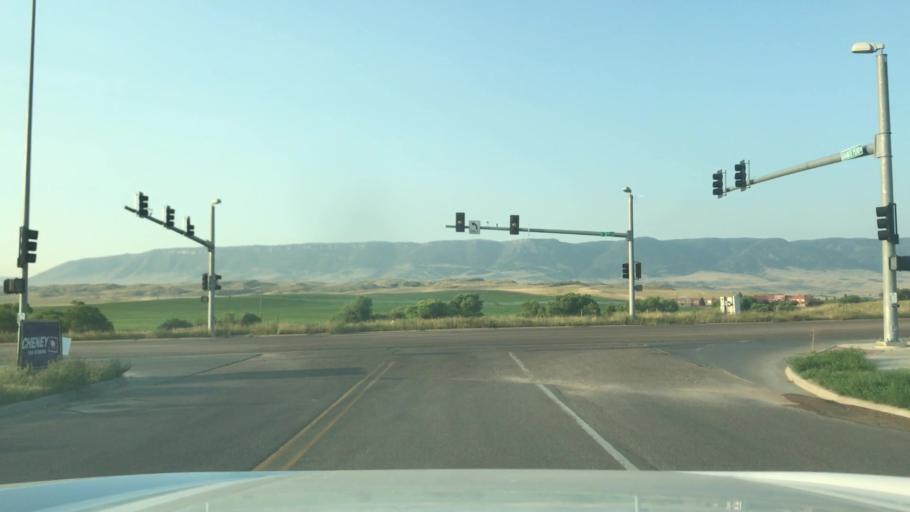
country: US
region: Wyoming
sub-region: Natrona County
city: Evansville
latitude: 42.8400
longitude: -106.2238
